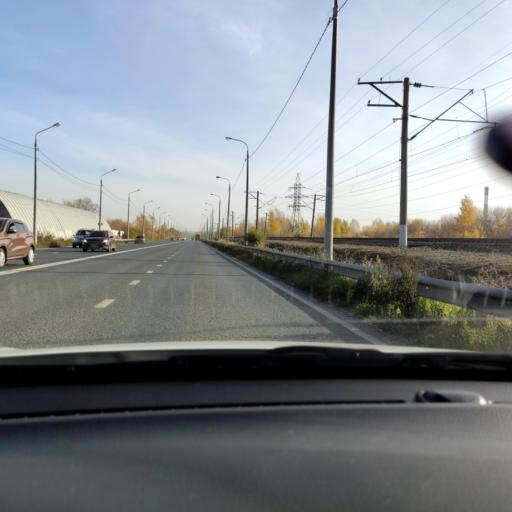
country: RU
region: Tatarstan
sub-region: Gorod Kazan'
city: Kazan
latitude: 55.8455
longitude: 49.1059
